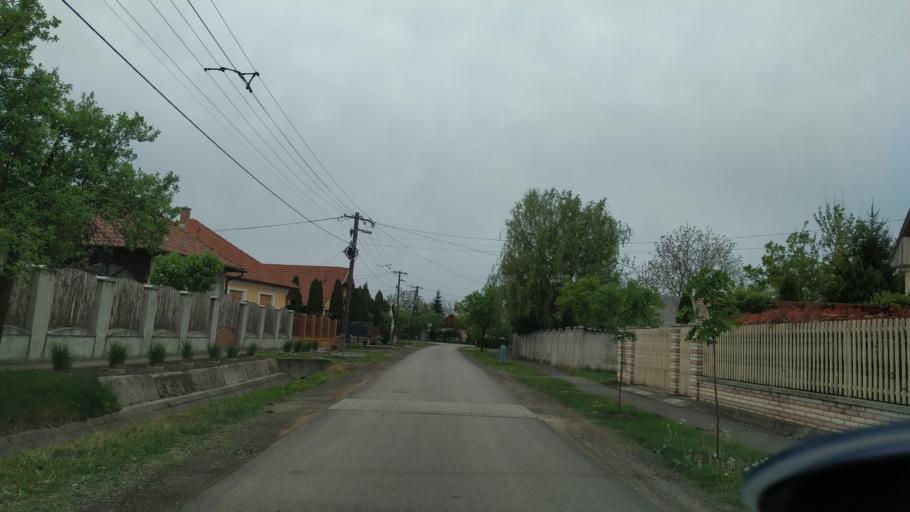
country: HU
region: Pest
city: Nagykata
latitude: 47.4189
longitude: 19.7361
